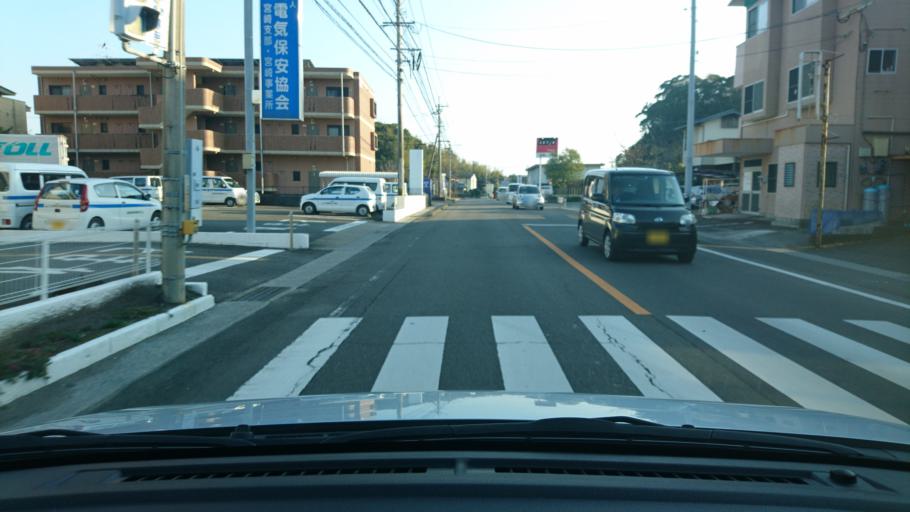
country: JP
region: Miyazaki
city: Miyazaki-shi
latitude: 31.9696
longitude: 131.4400
